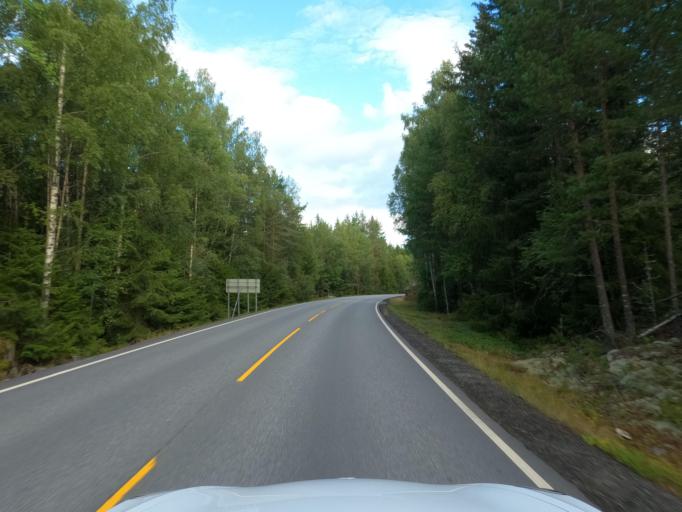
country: NO
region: Telemark
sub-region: Notodden
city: Notodden
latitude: 59.7275
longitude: 9.1614
